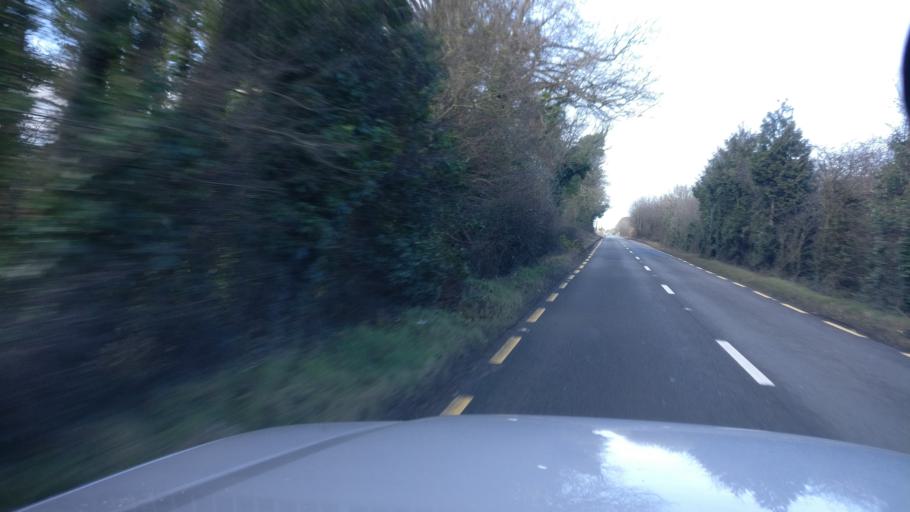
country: IE
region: Leinster
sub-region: Laois
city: Mountmellick
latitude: 53.0804
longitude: -7.3314
